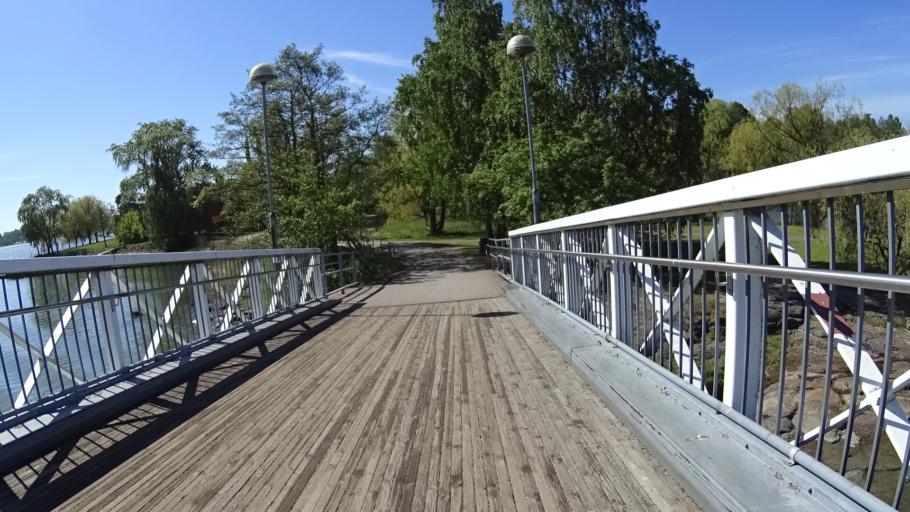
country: FI
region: Uusimaa
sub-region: Helsinki
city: Teekkarikylae
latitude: 60.1714
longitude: 24.8613
